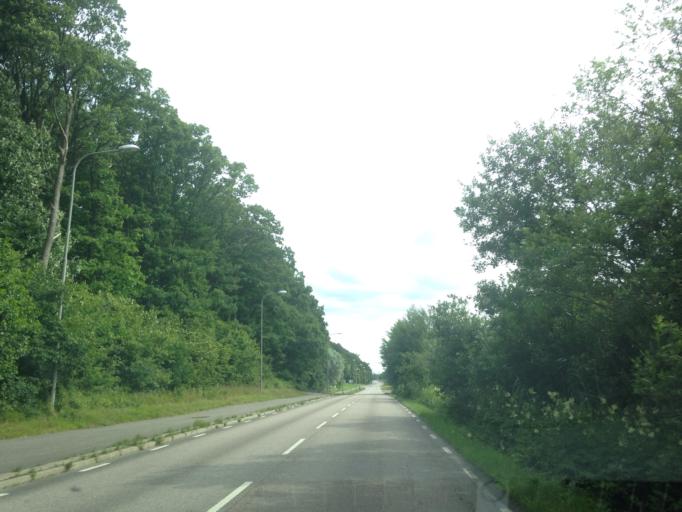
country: SE
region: Vaestra Goetaland
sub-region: Goteborg
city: Goeteborg
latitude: 57.7596
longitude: 11.9456
